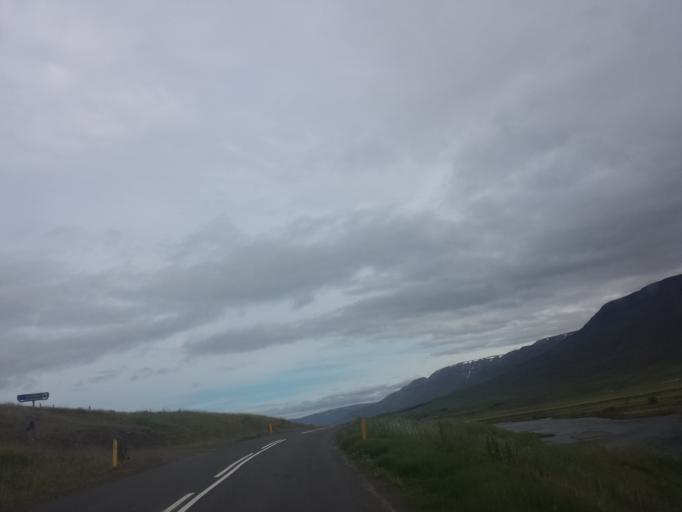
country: IS
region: Northeast
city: Akureyri
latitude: 65.4476
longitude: -18.2073
